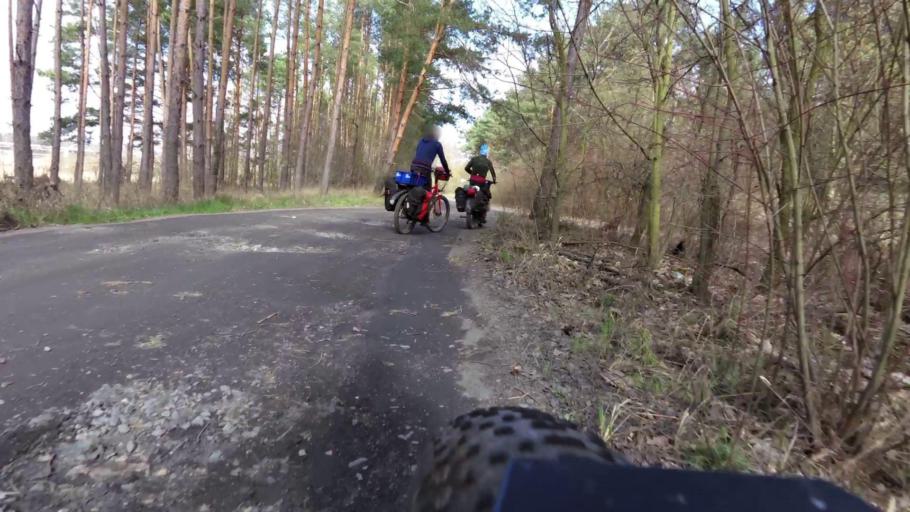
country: PL
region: Lubusz
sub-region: Powiat slubicki
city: Slubice
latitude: 52.3184
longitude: 14.5835
